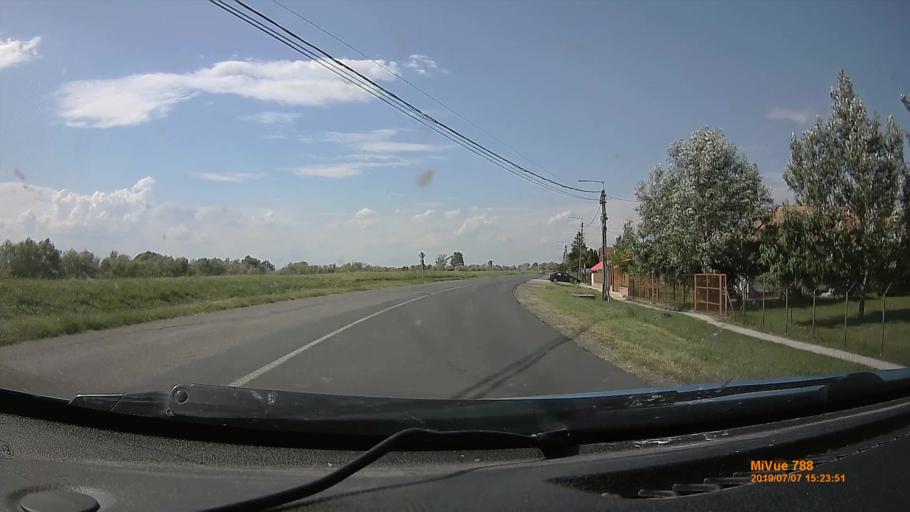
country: HU
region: Jasz-Nagykun-Szolnok
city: Janoshida
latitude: 47.3884
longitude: 20.0604
